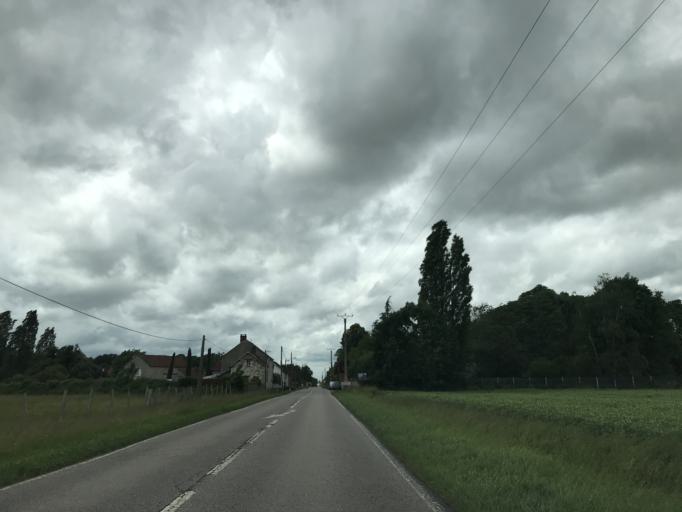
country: FR
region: Ile-de-France
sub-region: Departement des Yvelines
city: Breval
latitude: 48.9609
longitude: 1.5354
